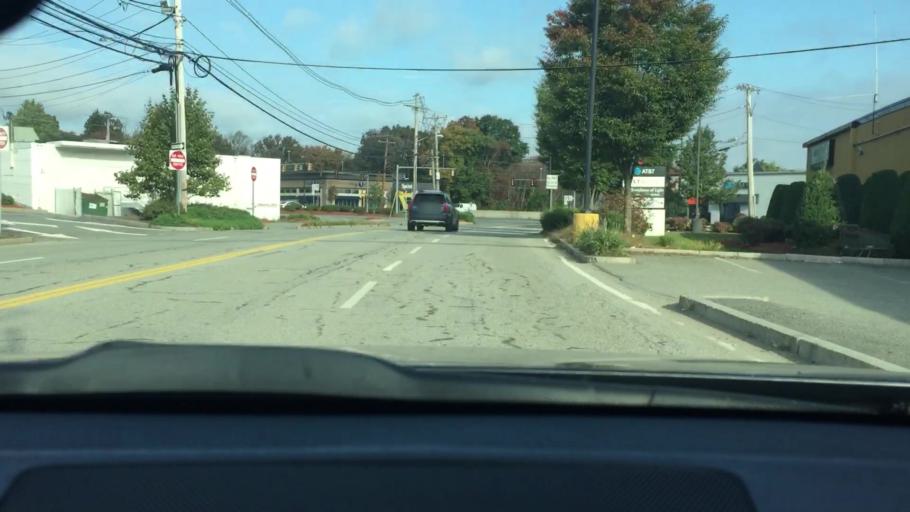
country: US
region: Massachusetts
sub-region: Norfolk County
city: Dedham
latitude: 42.2343
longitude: -71.1783
